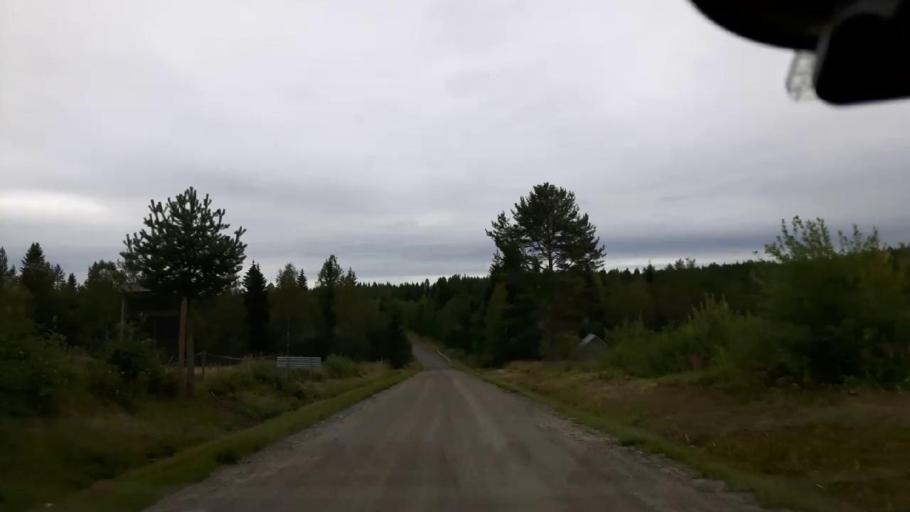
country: SE
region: Vaesternorrland
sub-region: Ange Kommun
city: Fransta
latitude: 62.8657
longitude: 15.9848
